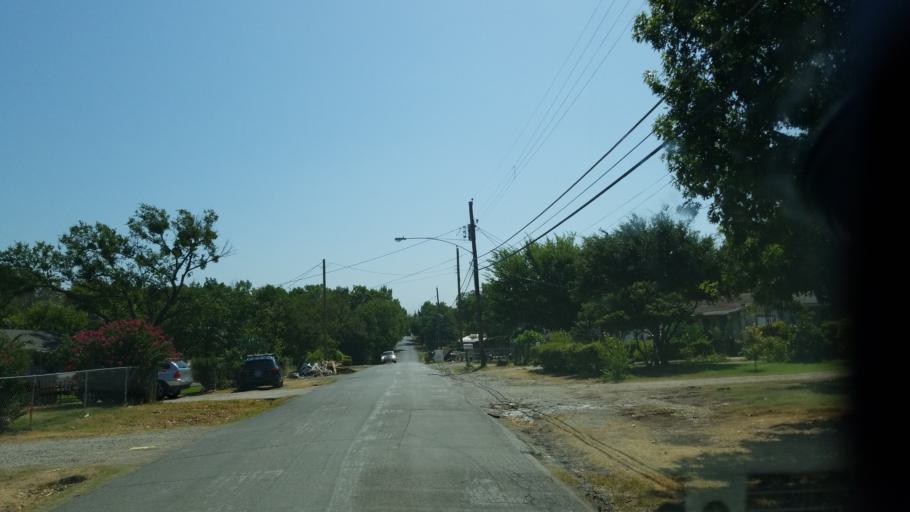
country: US
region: Texas
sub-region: Dallas County
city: Cockrell Hill
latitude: 32.7138
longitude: -96.9057
